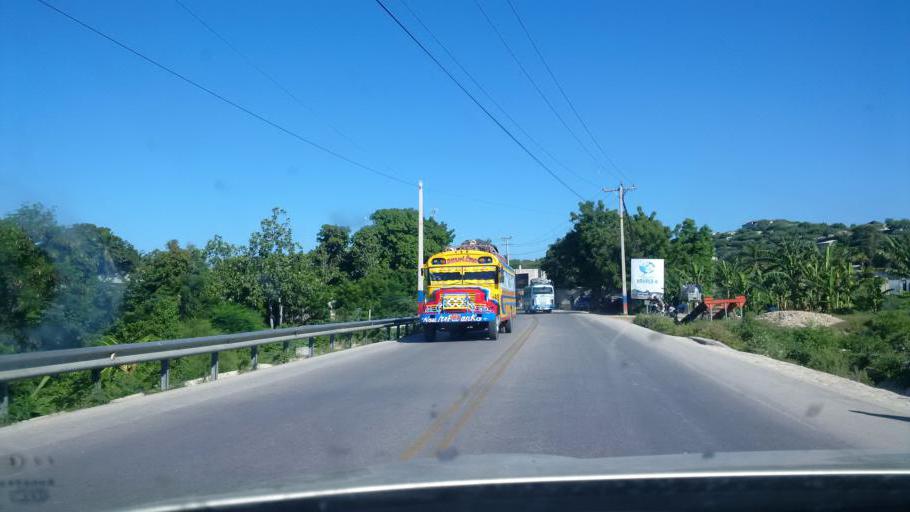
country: HT
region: Ouest
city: Cabaret
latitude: 18.7381
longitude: -72.4094
